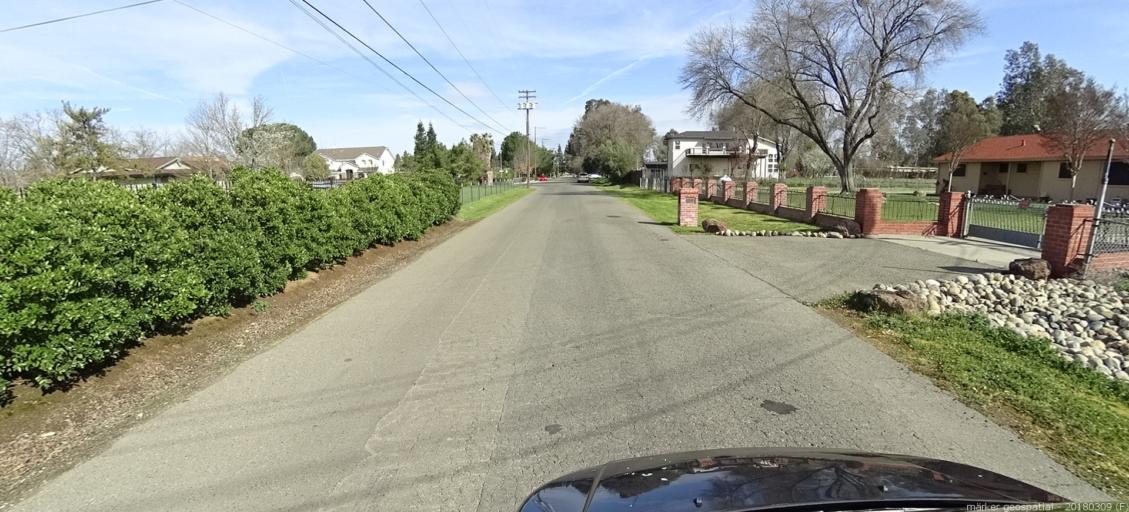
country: US
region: California
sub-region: Sacramento County
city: Florin
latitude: 38.4562
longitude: -121.3902
